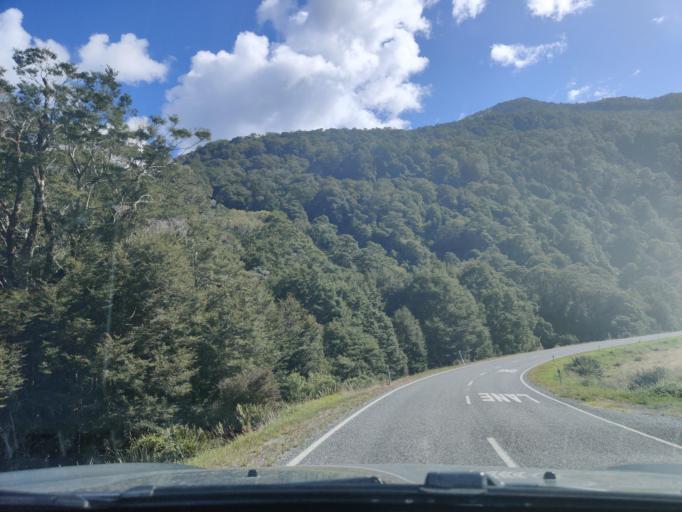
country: NZ
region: Otago
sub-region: Queenstown-Lakes District
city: Wanaka
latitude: -44.0110
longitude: 169.3813
